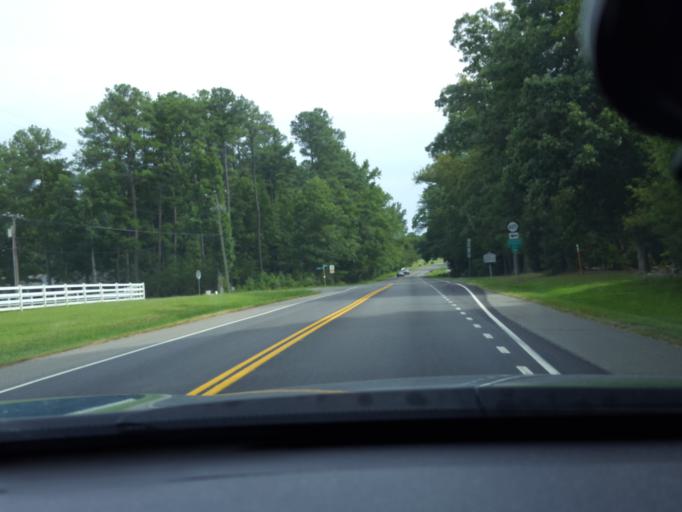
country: US
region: Virginia
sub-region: Hanover County
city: Hanover
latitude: 37.7477
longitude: -77.3594
